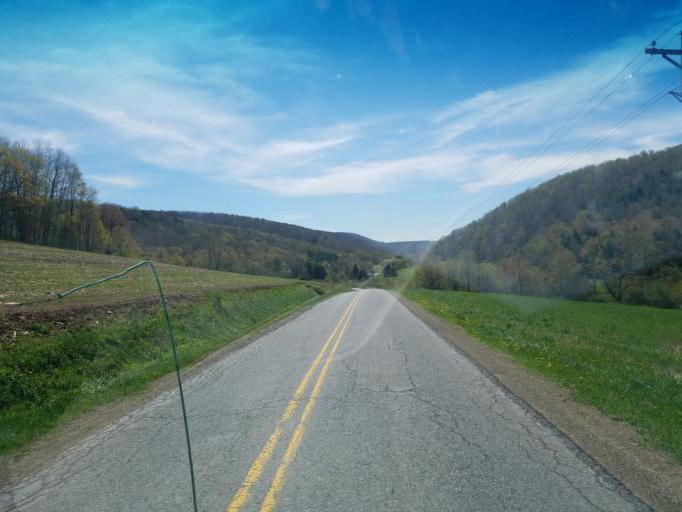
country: US
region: Pennsylvania
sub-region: Potter County
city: Galeton
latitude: 41.8797
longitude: -77.7342
